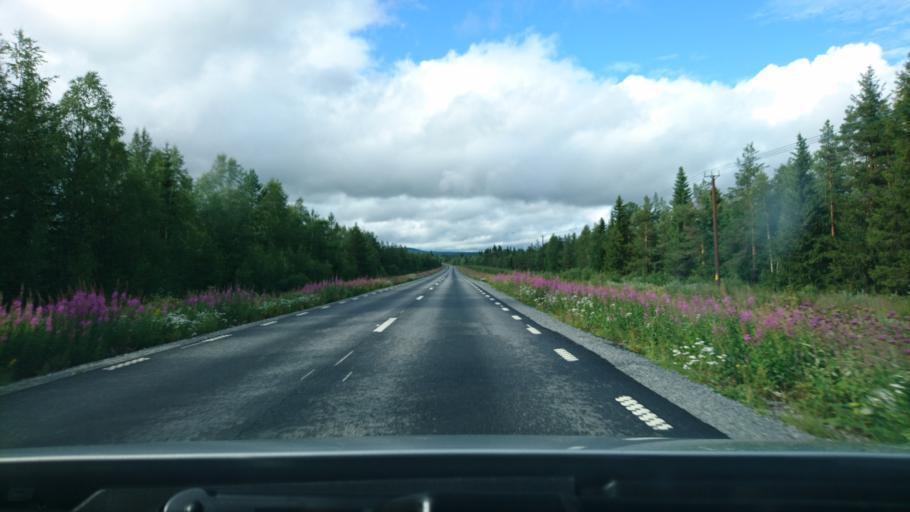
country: SE
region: Vaesterbotten
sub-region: Vilhelmina Kommun
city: Vilhelmina
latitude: 64.7242
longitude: 16.7080
